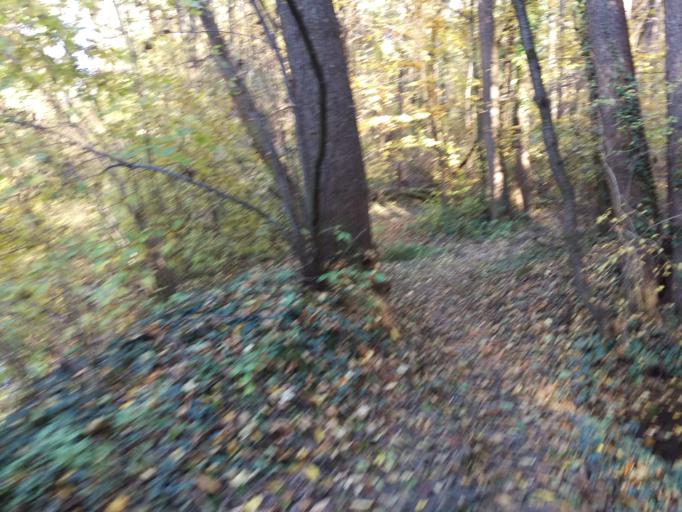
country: AT
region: Styria
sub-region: Graz Stadt
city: Graz
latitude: 47.0609
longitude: 15.4756
